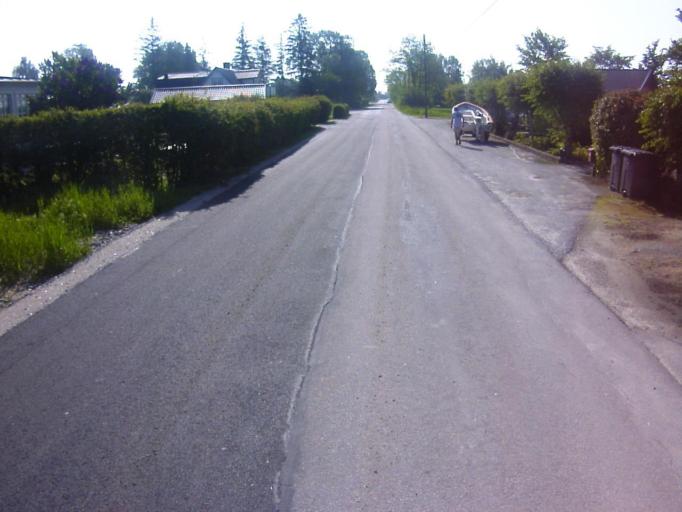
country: SE
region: Blekinge
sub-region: Solvesborgs Kommun
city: Soelvesborg
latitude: 56.0477
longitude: 14.6603
